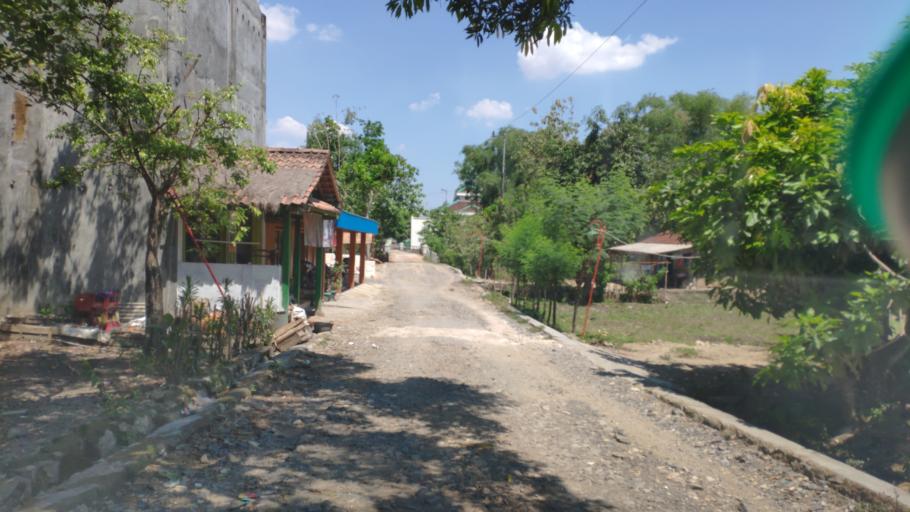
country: ID
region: Central Java
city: Galuk
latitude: -7.1086
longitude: 111.5005
